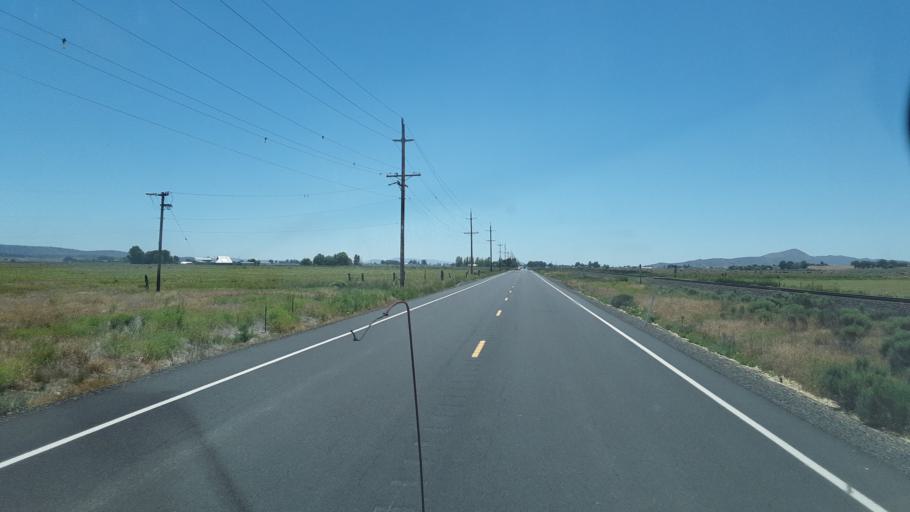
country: US
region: Oregon
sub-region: Klamath County
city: Altamont
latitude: 42.0595
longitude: -121.6505
